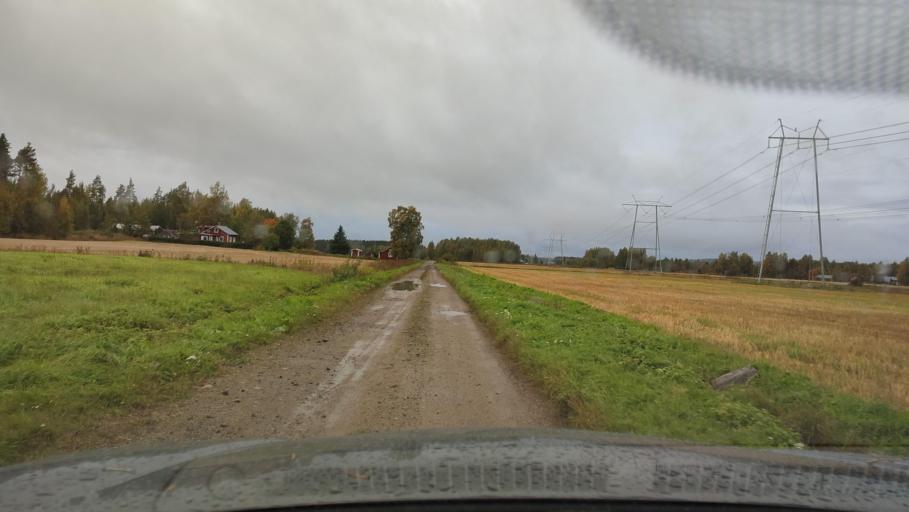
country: FI
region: Southern Ostrobothnia
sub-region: Suupohja
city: Karijoki
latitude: 62.2236
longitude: 21.6237
